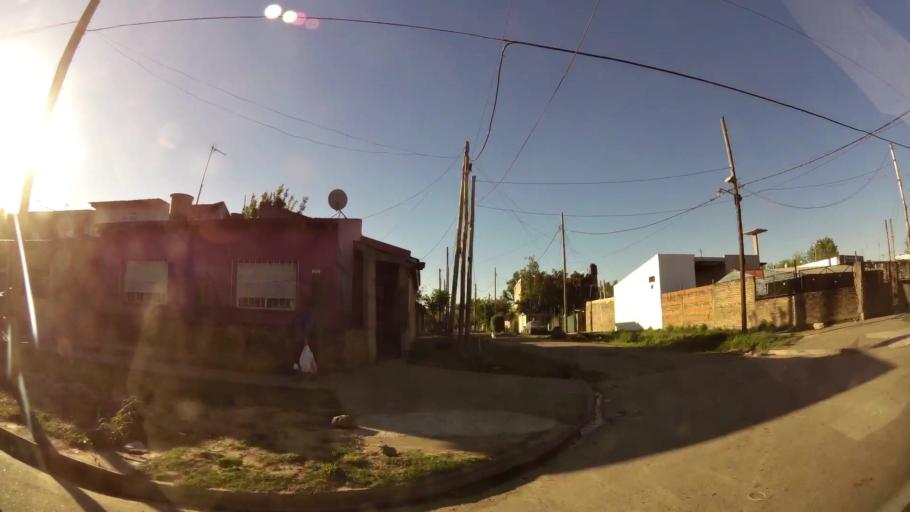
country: AR
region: Buenos Aires
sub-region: Partido de Almirante Brown
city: Adrogue
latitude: -34.7689
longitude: -58.3284
